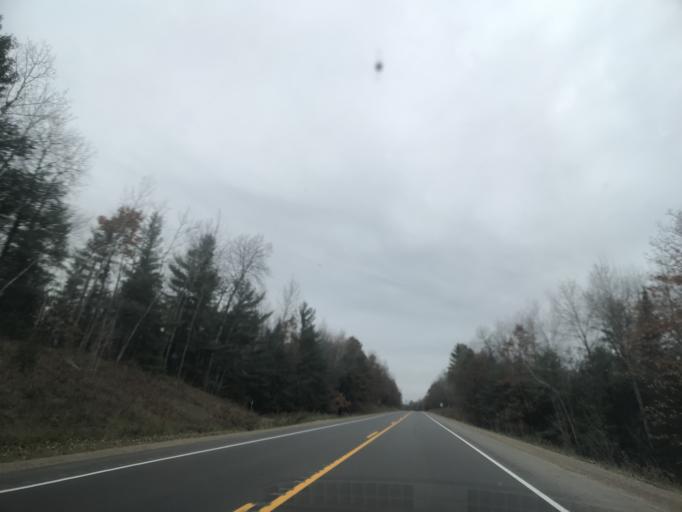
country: US
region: Wisconsin
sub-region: Menominee County
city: Legend Lake
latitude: 45.2670
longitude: -88.5112
